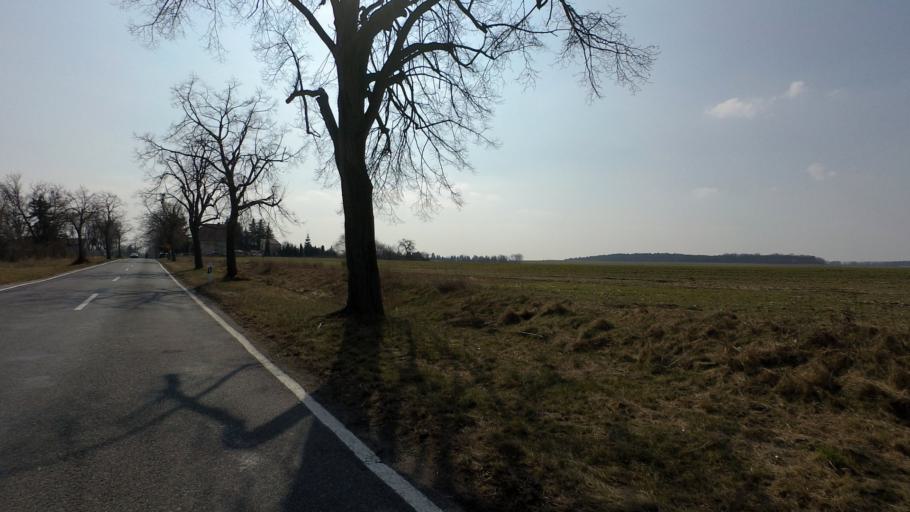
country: DE
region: Brandenburg
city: Gross Kreutz
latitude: 52.4222
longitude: 12.7906
